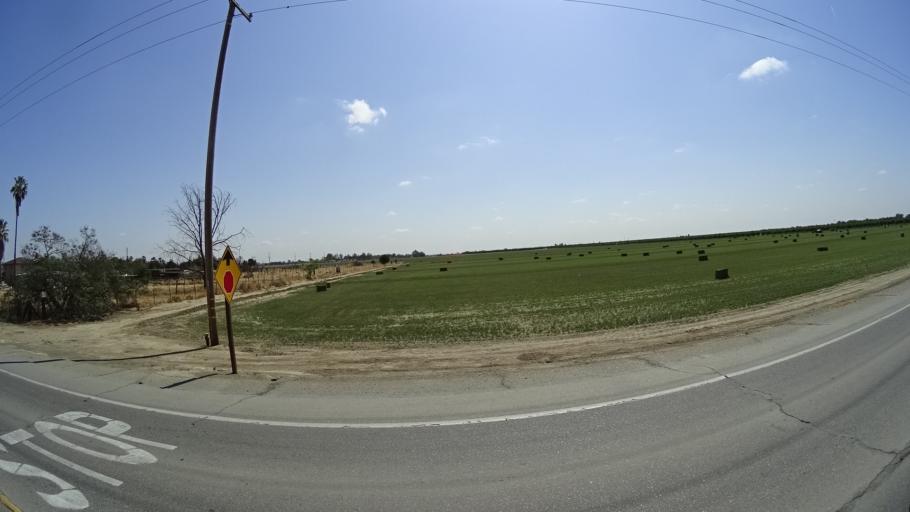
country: US
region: California
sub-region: Kings County
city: Home Garden
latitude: 36.2969
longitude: -119.6370
